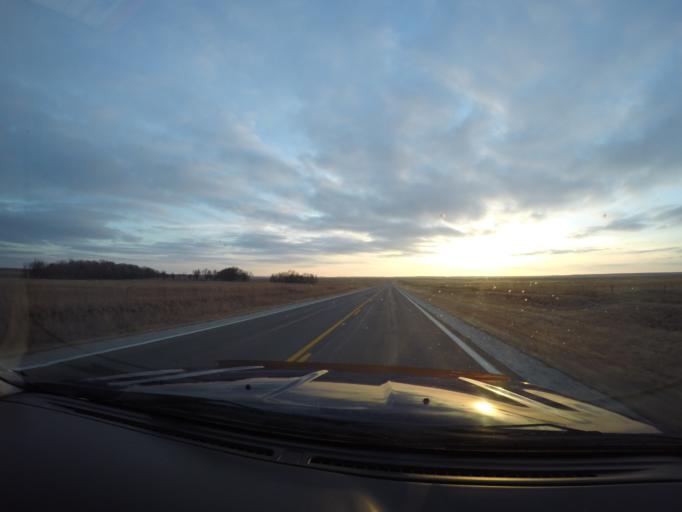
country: US
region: Kansas
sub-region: Chase County
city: Cottonwood Falls
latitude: 38.5183
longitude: -96.5375
